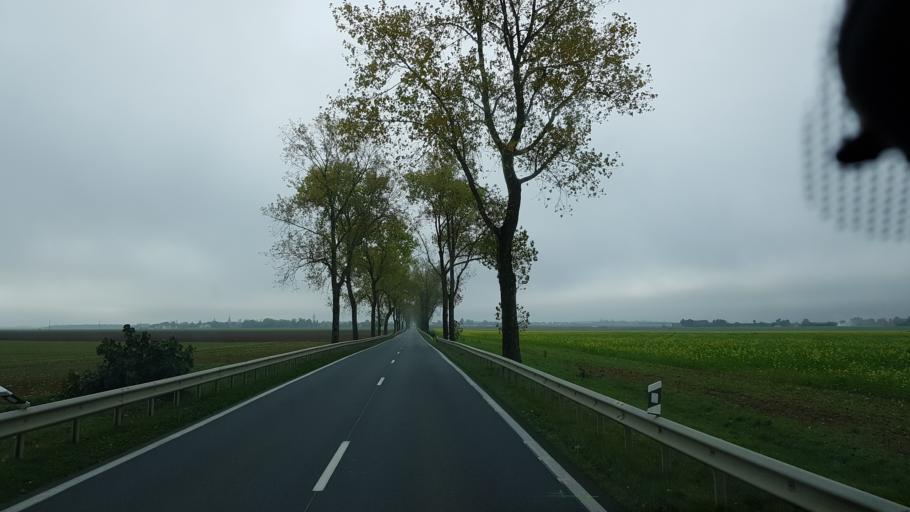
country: FR
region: Ile-de-France
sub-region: Departement de l'Essonne
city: Corbreuse
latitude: 48.4439
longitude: 1.9571
